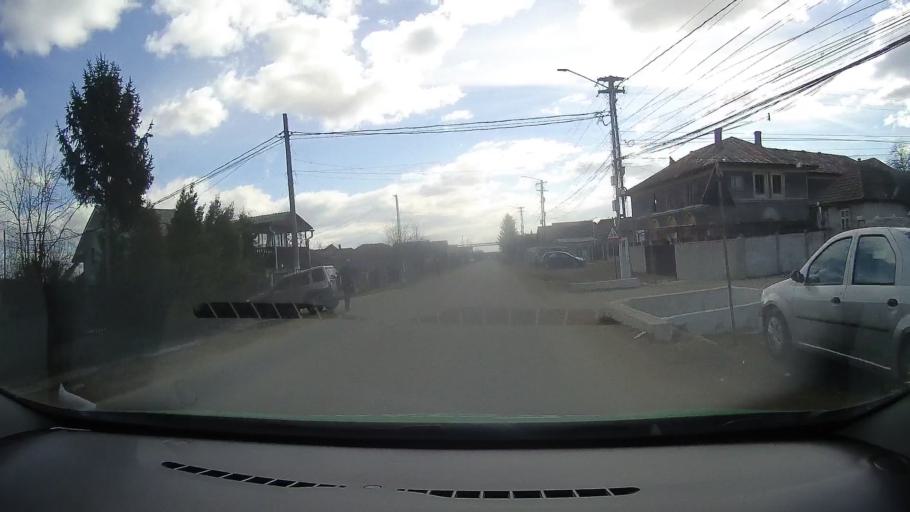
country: RO
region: Dambovita
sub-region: Comuna Doicesti
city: Doicesti
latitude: 44.9828
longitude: 25.3880
